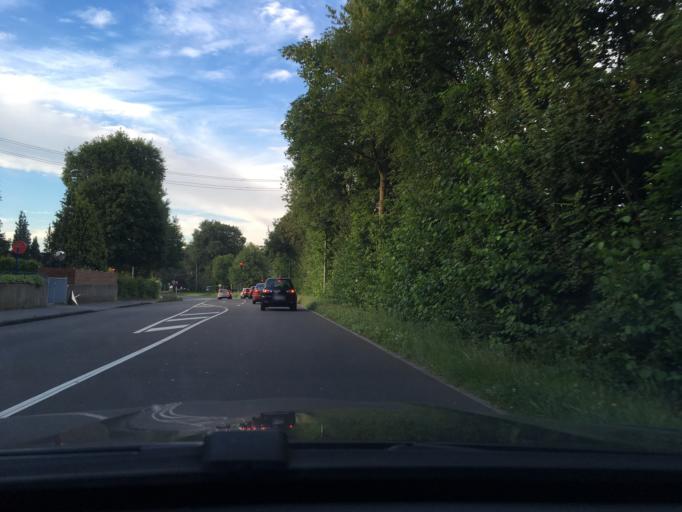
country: DE
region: North Rhine-Westphalia
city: Opladen
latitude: 51.0558
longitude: 7.0568
